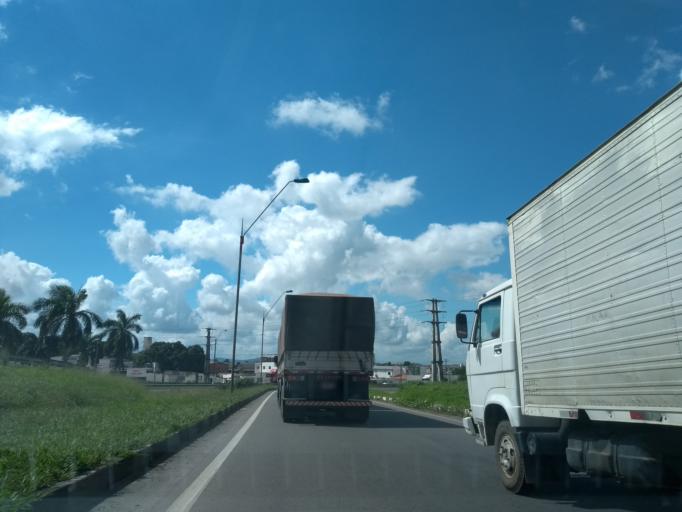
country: BR
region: Bahia
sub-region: Feira De Santana
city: Feira de Santana
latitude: -12.2732
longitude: -38.9354
